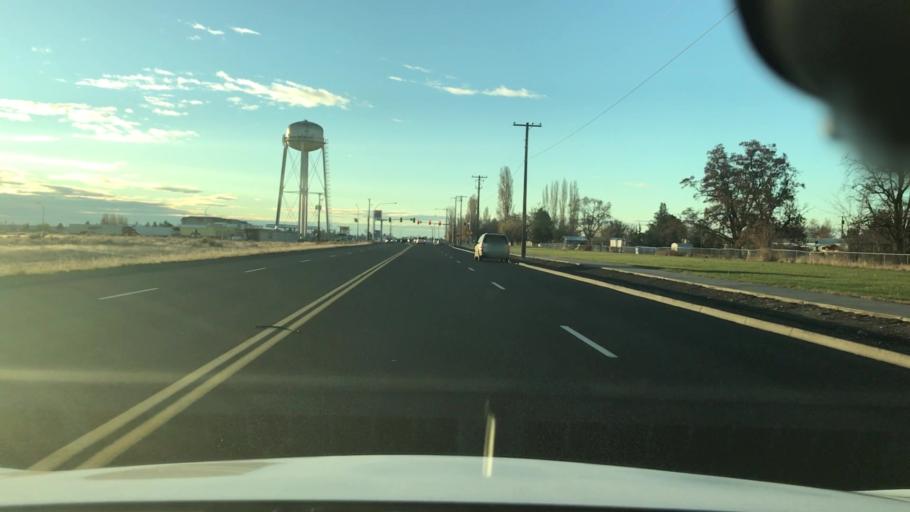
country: US
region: Washington
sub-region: Grant County
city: Moses Lake North
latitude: 47.1659
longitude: -119.3153
